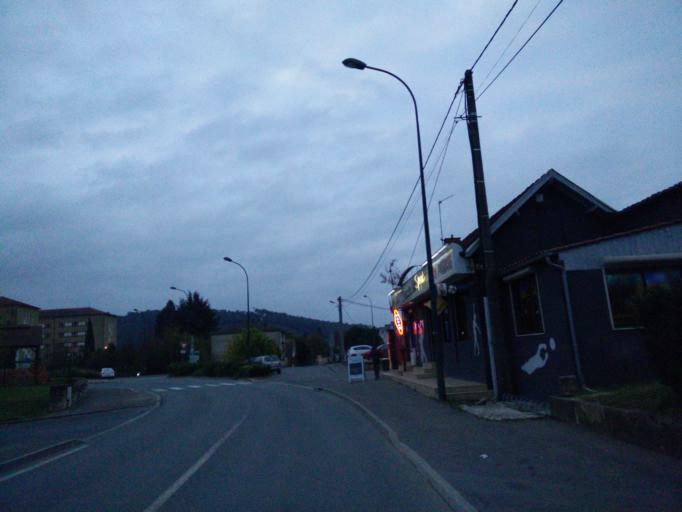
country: FR
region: Aquitaine
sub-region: Departement de la Dordogne
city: Sarlat-la-Caneda
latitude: 44.8746
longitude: 1.2295
